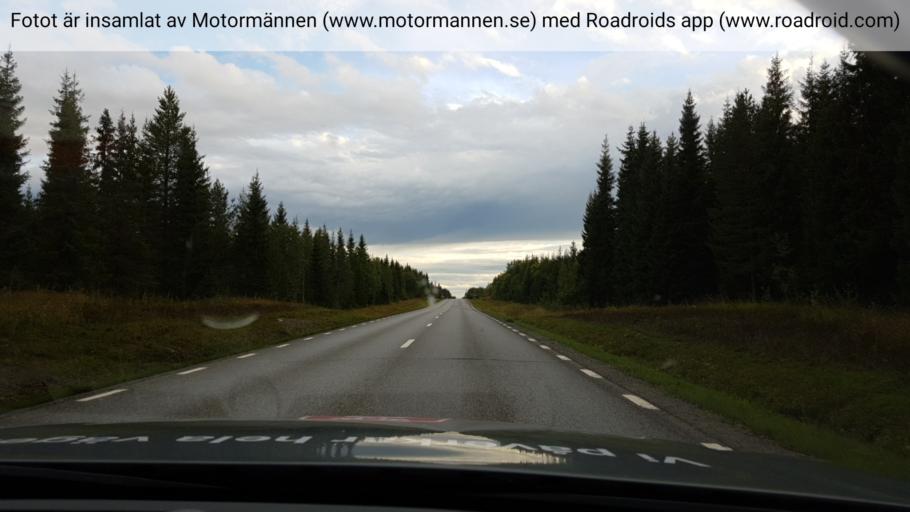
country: SE
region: Jaemtland
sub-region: Stroemsunds Kommun
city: Stroemsund
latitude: 63.7207
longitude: 15.4725
